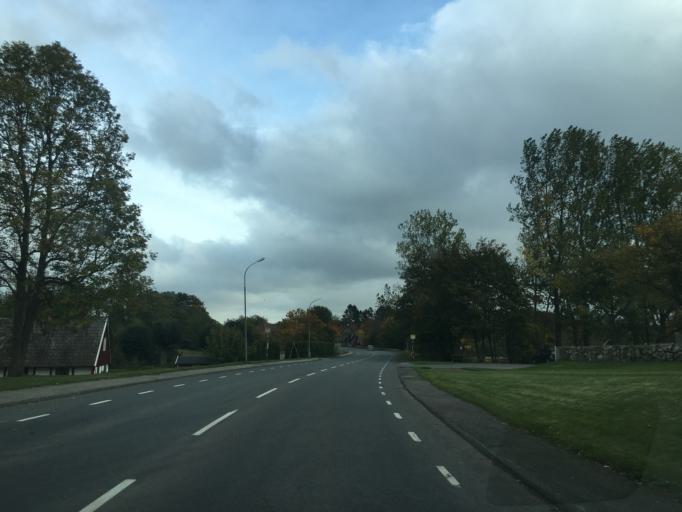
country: SE
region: Skane
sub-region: Simrishamns Kommun
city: Kivik
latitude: 55.6355
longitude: 14.1227
